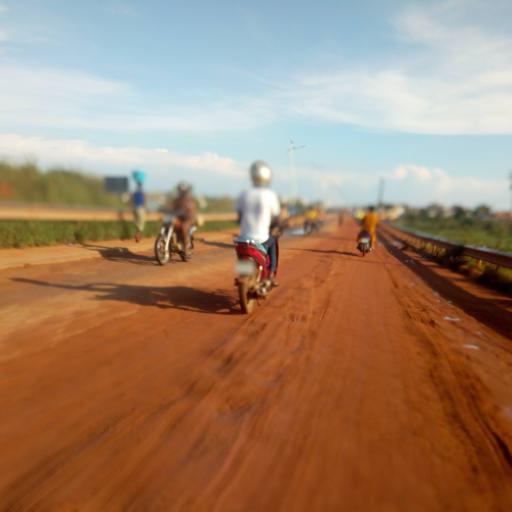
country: BJ
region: Atlantique
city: Hevie
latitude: 6.3979
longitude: 2.2696
